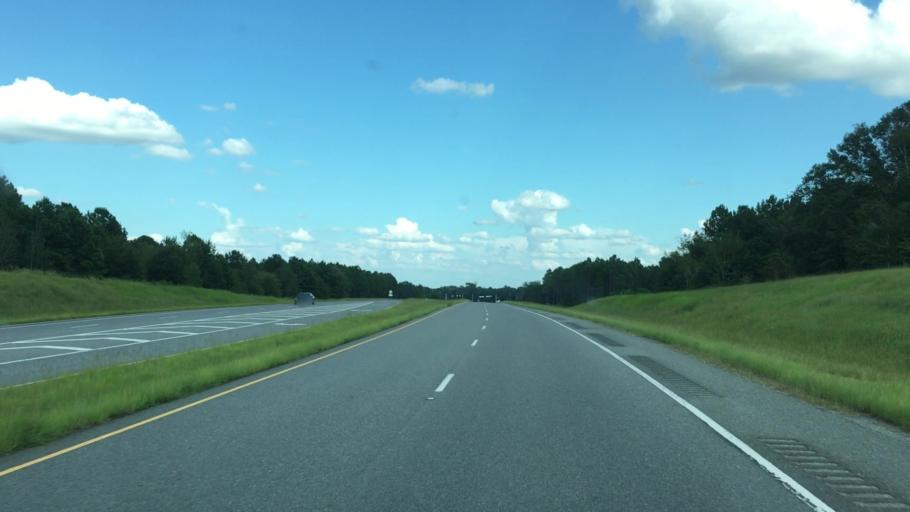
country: US
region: Georgia
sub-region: Laurens County
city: Dublin
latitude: 32.5017
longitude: -82.9387
